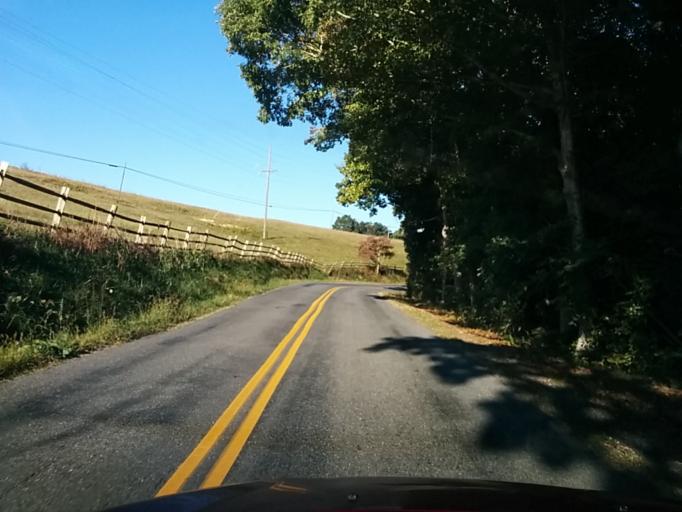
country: US
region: Virginia
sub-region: City of Lexington
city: Lexington
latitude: 37.7440
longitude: -79.5403
